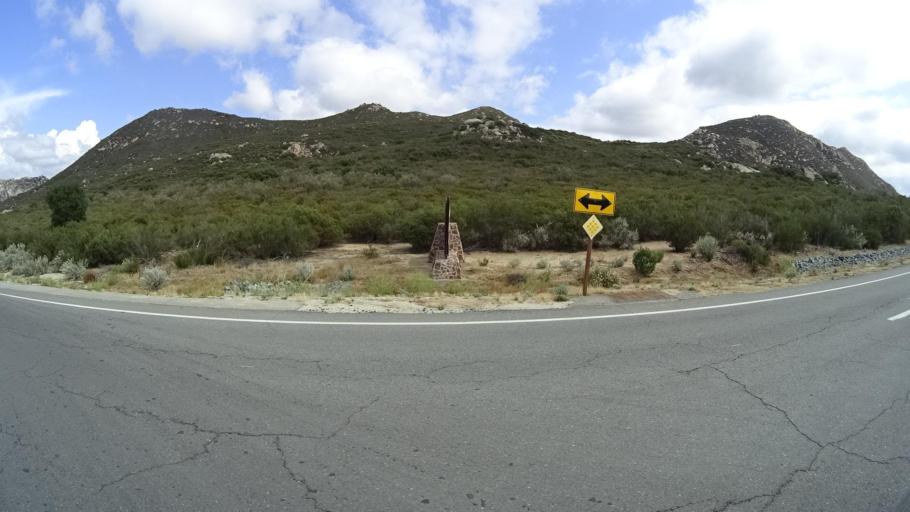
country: US
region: California
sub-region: San Diego County
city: Campo
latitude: 32.6906
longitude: -116.4894
